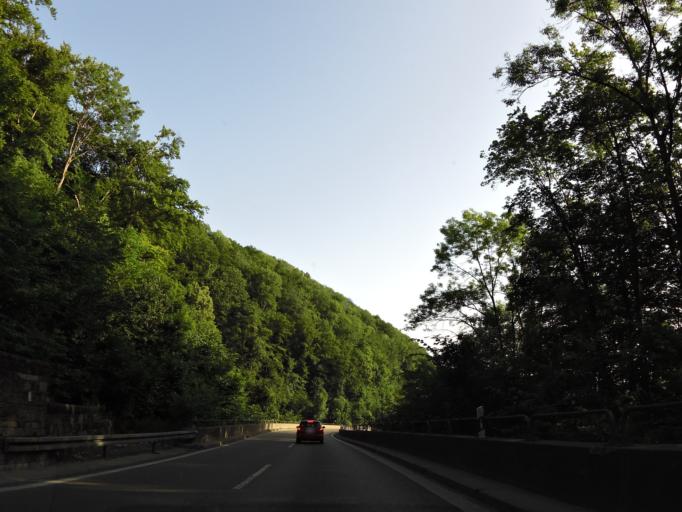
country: DE
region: Baden-Wuerttemberg
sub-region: Regierungsbezirk Stuttgart
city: Muhlhausen
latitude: 48.5652
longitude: 9.6747
